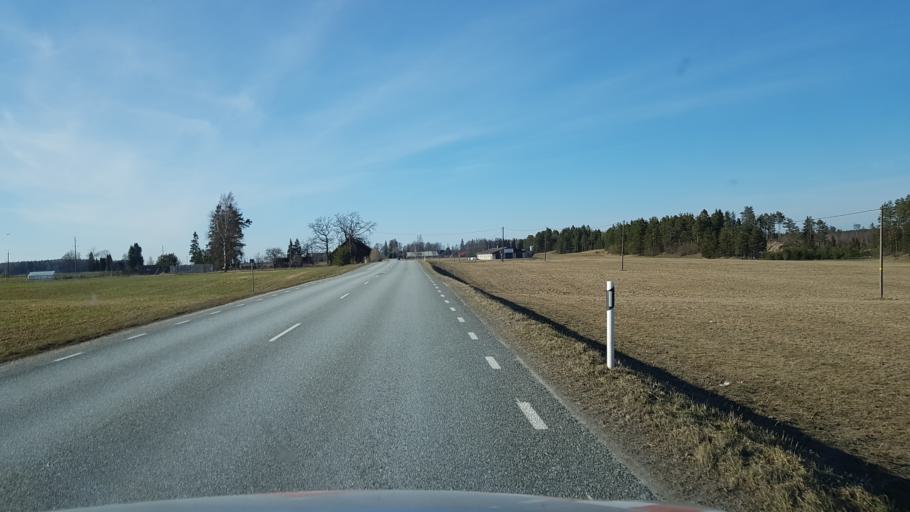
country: EE
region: Laeaene-Virumaa
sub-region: Vinni vald
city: Vinni
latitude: 59.1989
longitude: 26.5621
